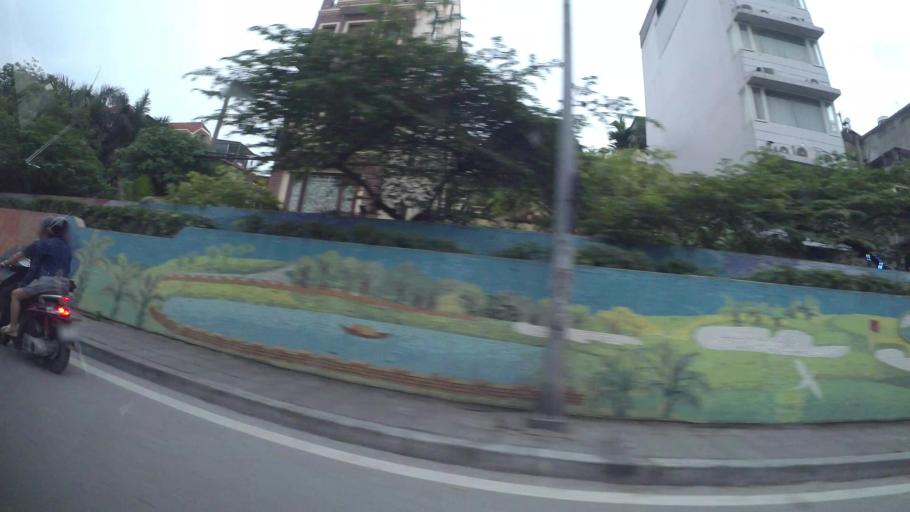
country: VN
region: Ha Noi
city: Hoan Kiem
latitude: 21.0212
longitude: 105.8618
